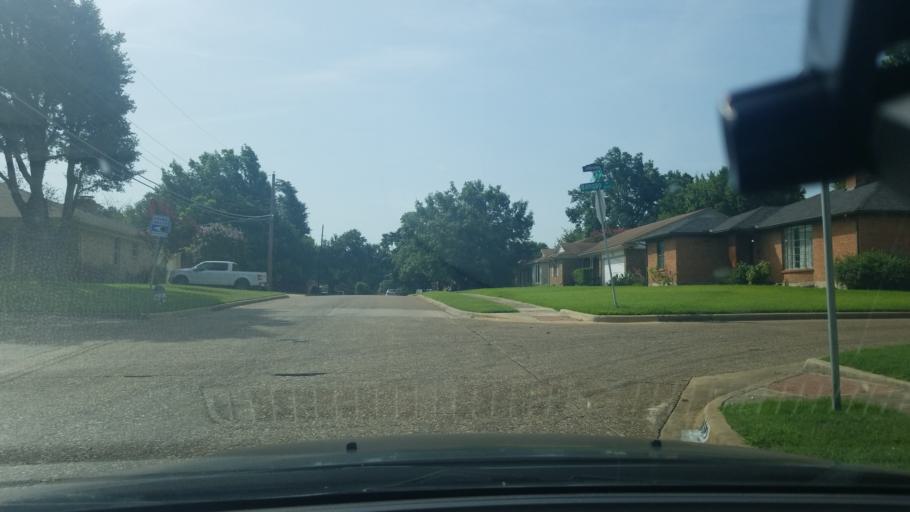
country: US
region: Texas
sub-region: Dallas County
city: Highland Park
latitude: 32.8055
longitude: -96.7057
